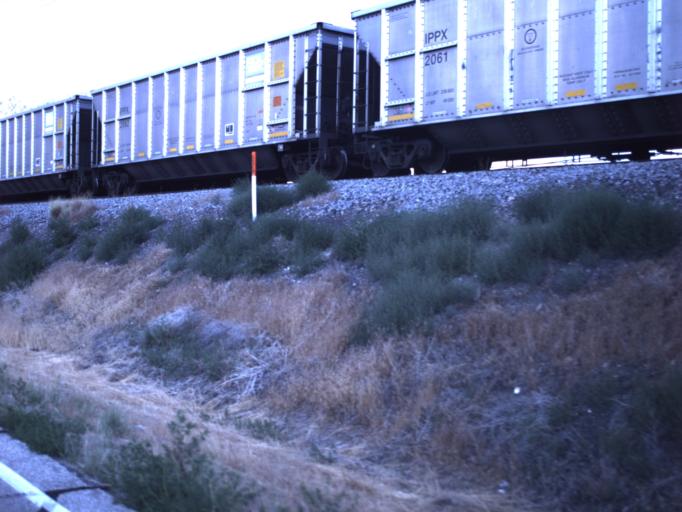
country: US
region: Utah
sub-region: Carbon County
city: Helper
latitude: 39.6784
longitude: -110.8567
